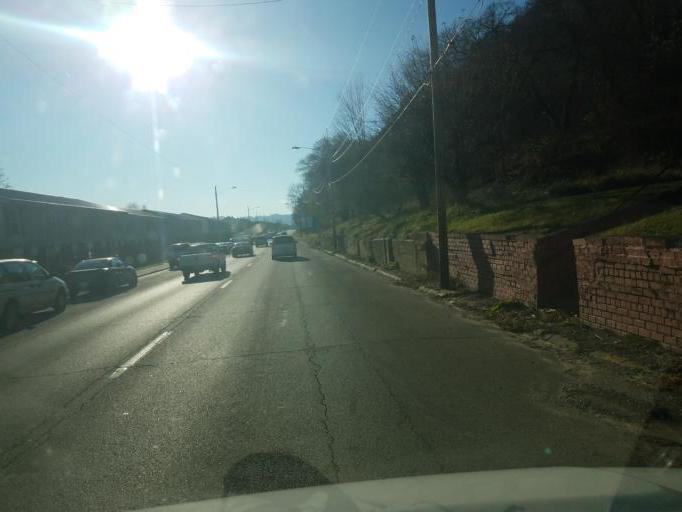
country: US
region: Ohio
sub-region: Scioto County
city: New Boston
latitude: 38.7502
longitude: -82.9412
